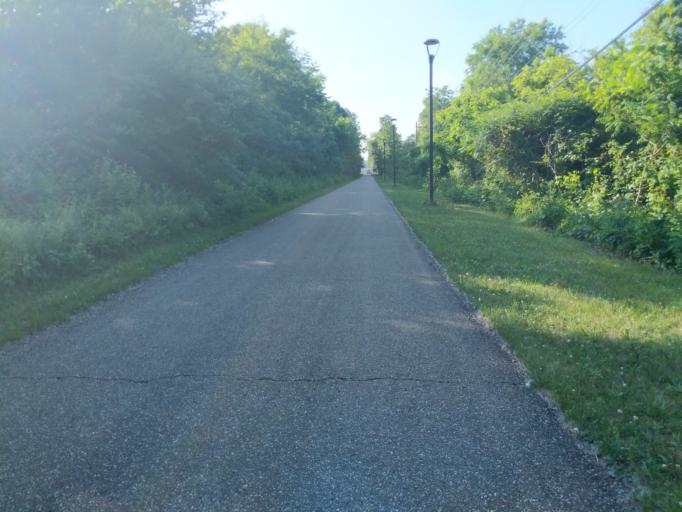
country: US
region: Ohio
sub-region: Athens County
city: Nelsonville
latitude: 39.4374
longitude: -82.2169
